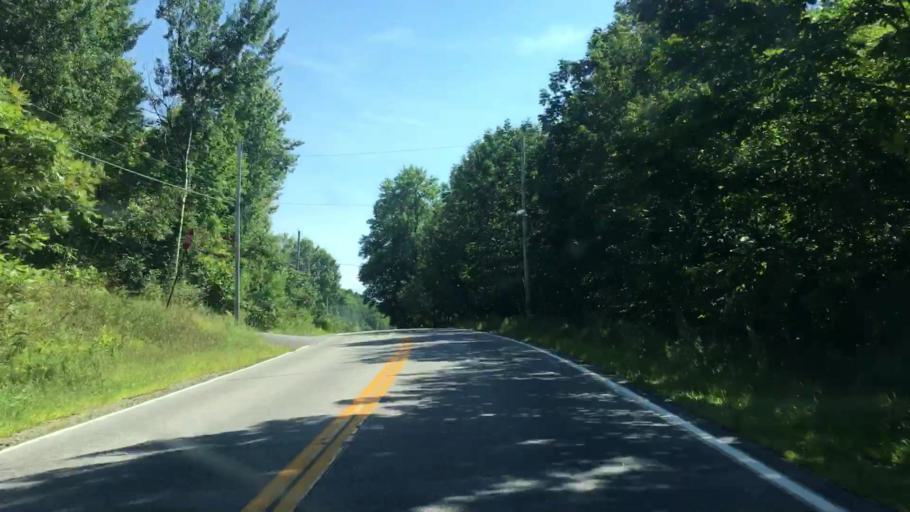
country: US
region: Maine
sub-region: Androscoggin County
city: Sabattus
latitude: 44.1404
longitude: -70.0877
